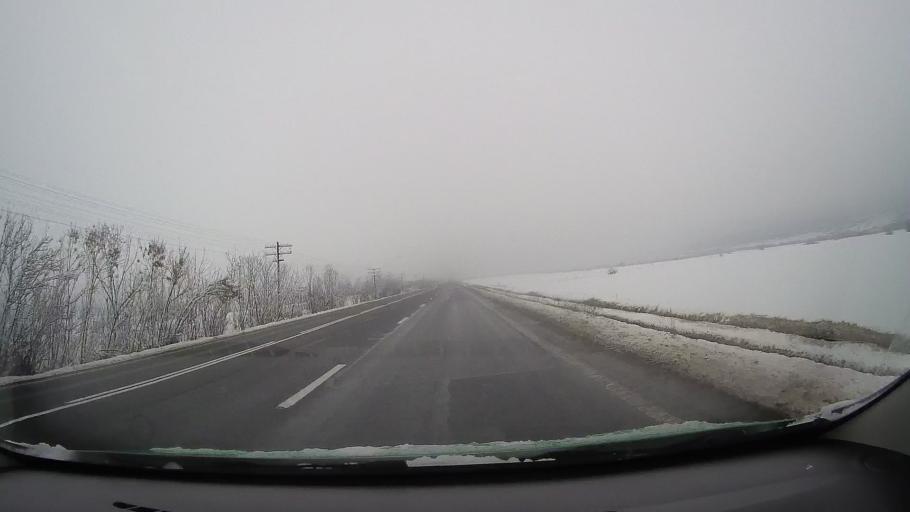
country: RO
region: Sibiu
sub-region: Oras Saliste
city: Saliste
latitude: 45.7967
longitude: 23.9086
